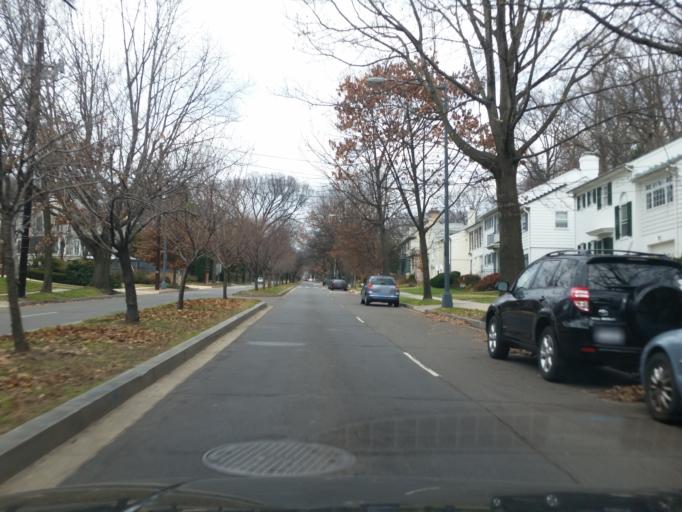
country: US
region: Washington, D.C.
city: Washington, D.C.
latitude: 38.9248
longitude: -77.0597
